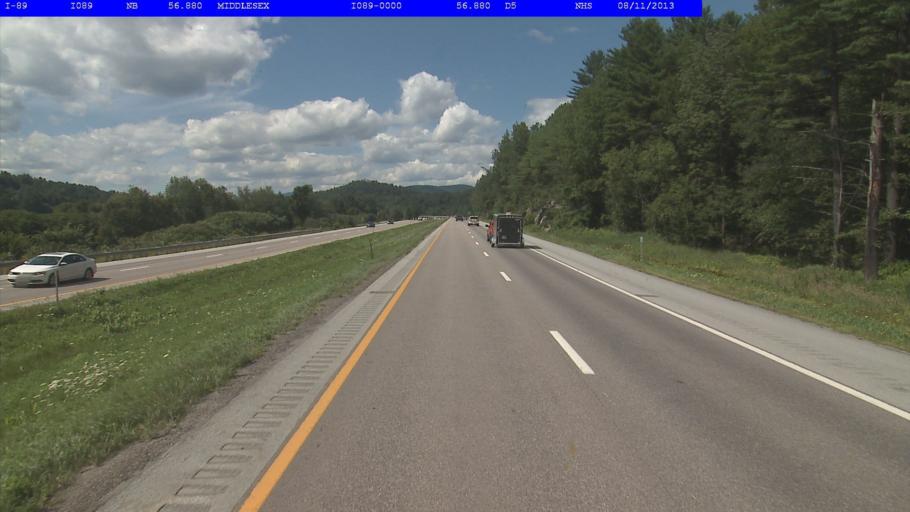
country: US
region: Vermont
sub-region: Washington County
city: Montpelier
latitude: 44.2810
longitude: -72.6593
